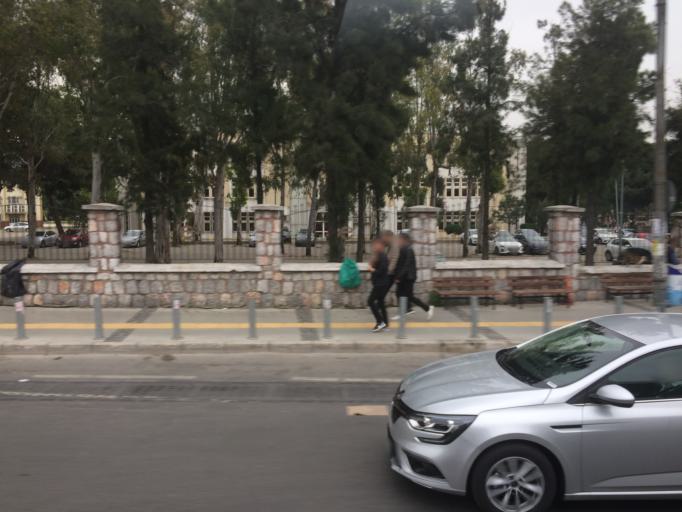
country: TR
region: Izmir
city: Bornova
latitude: 38.4580
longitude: 27.2107
